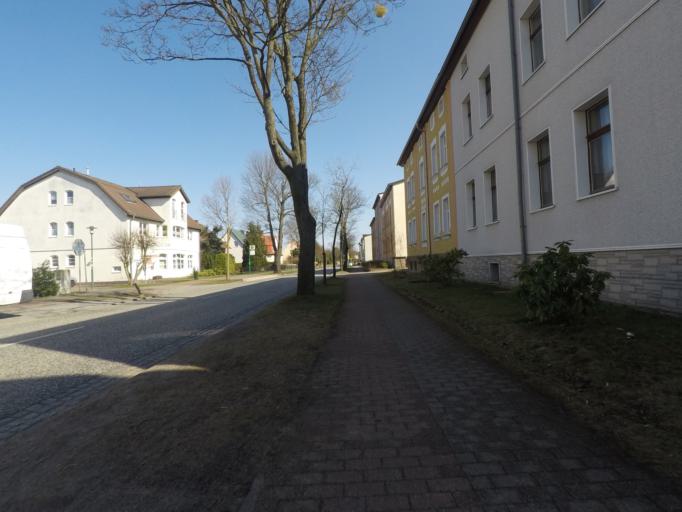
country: DE
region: Brandenburg
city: Britz
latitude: 52.8609
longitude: 13.7512
